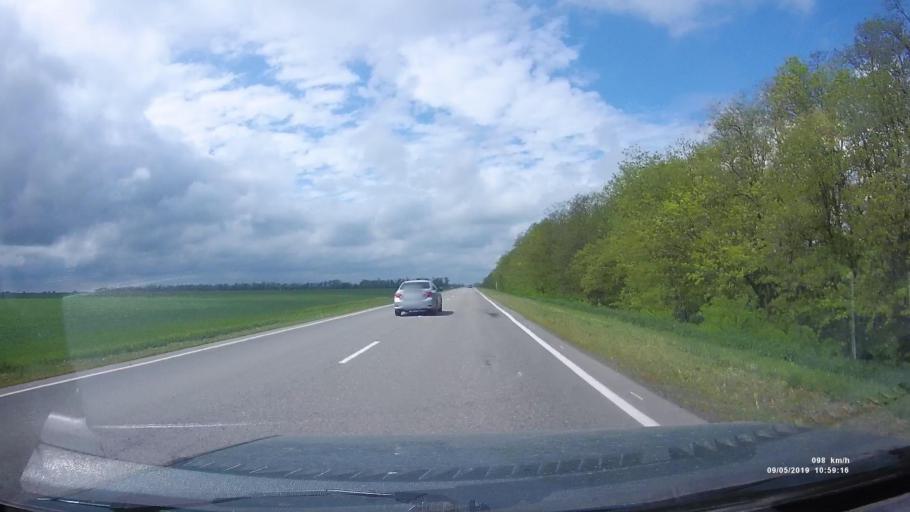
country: RU
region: Rostov
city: Peshkovo
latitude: 46.8579
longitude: 39.2431
